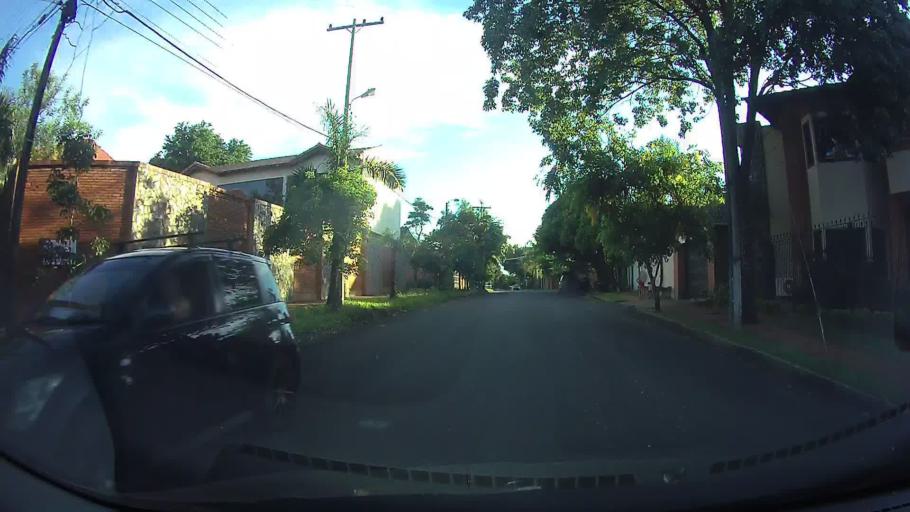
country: PY
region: Central
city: San Lorenzo
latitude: -25.2664
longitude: -57.5082
